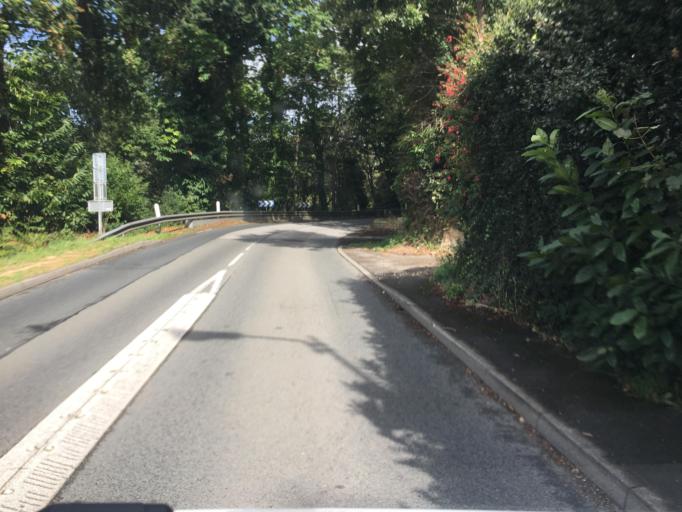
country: FR
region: Brittany
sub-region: Departement du Finistere
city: La Foret-Fouesnant
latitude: 47.9143
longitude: -3.9739
